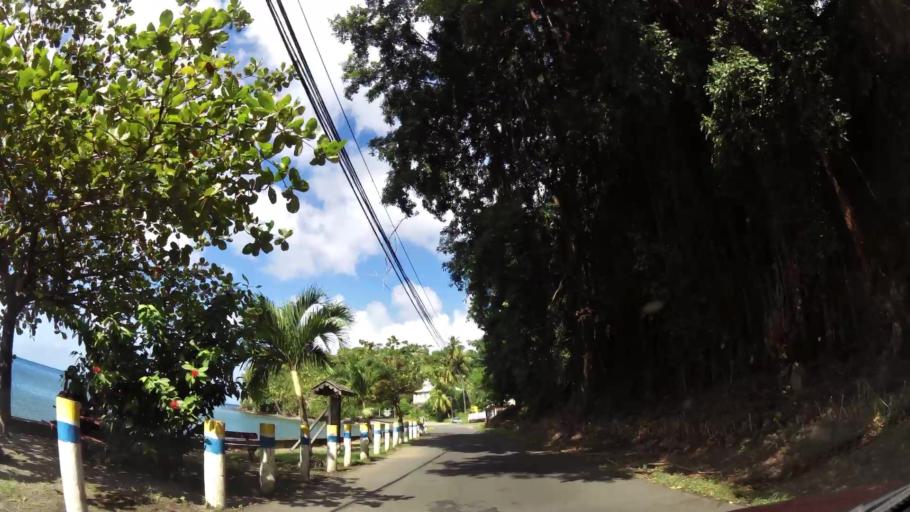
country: DM
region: Saint John
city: Portsmouth
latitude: 15.6108
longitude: -61.4643
